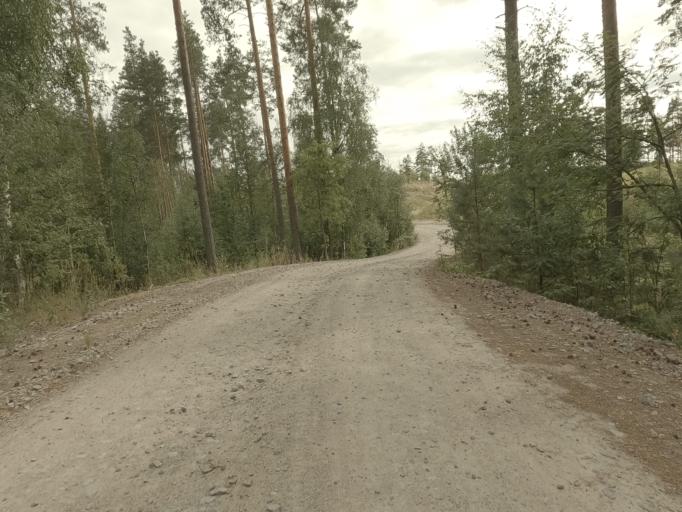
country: RU
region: Leningrad
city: Kamennogorsk
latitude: 60.9781
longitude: 29.1720
